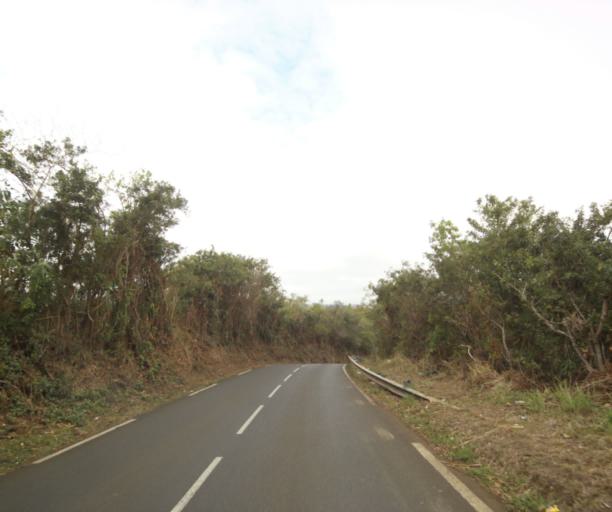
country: RE
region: Reunion
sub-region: Reunion
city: Trois-Bassins
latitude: -21.0641
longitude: 55.2800
